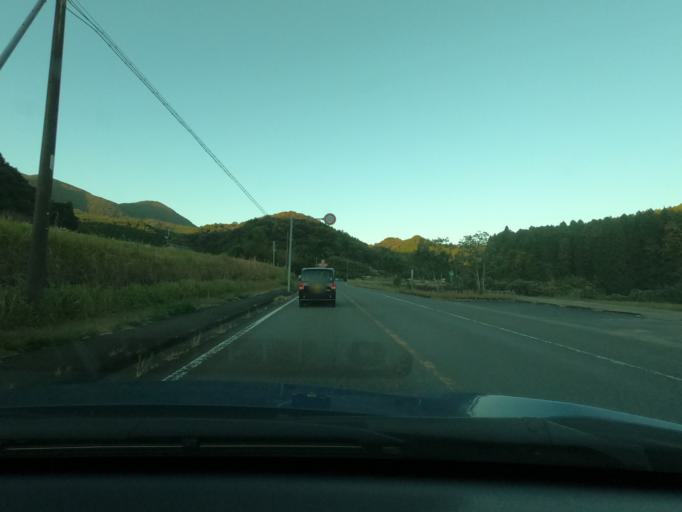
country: JP
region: Kagoshima
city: Satsumasendai
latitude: 31.7946
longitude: 130.4725
